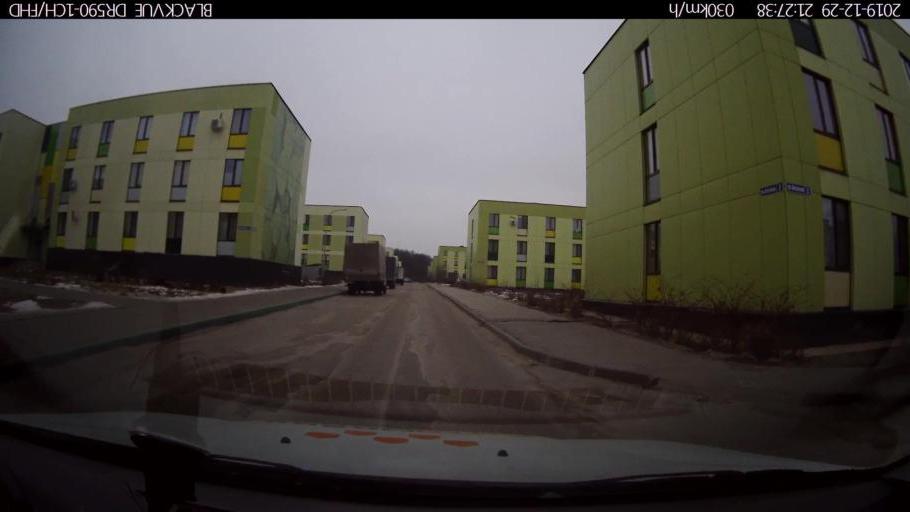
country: RU
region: Nizjnij Novgorod
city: Afonino
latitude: 56.2137
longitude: 44.0226
